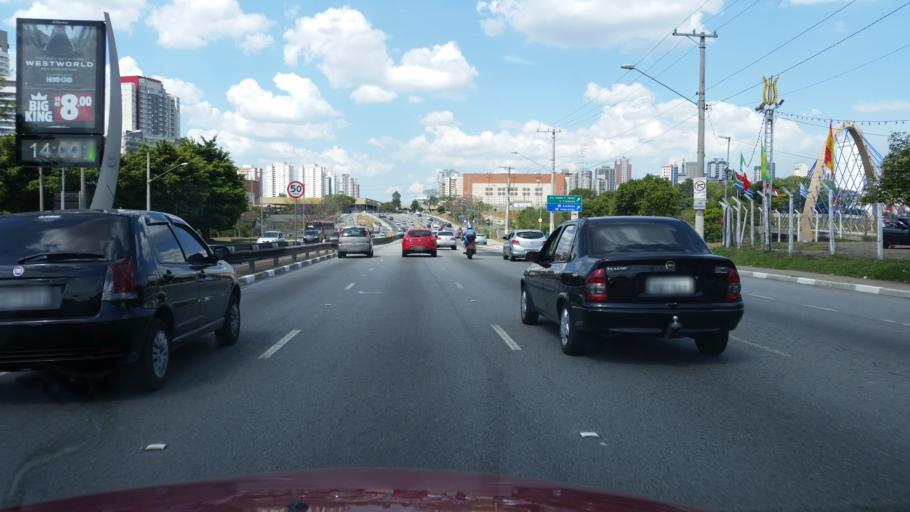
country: BR
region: Sao Paulo
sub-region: Sao Paulo
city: Sao Paulo
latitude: -23.5425
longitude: -46.5828
